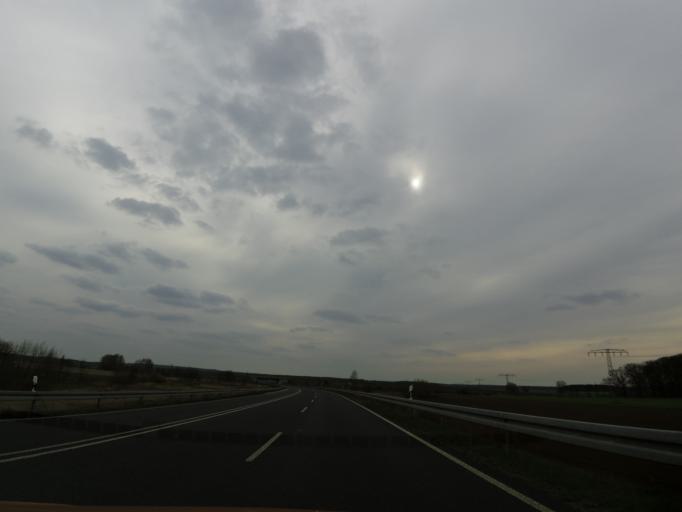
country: DE
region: Brandenburg
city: Mullrose
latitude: 52.2564
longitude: 14.3998
